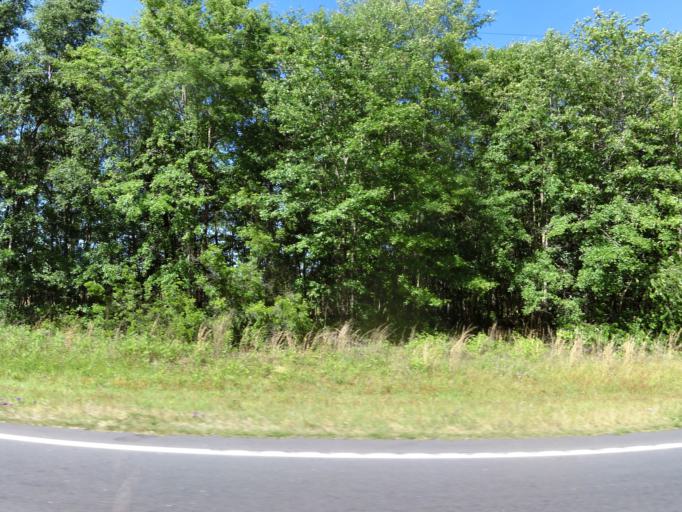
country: US
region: South Carolina
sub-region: Barnwell County
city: Williston
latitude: 33.4144
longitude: -81.4696
